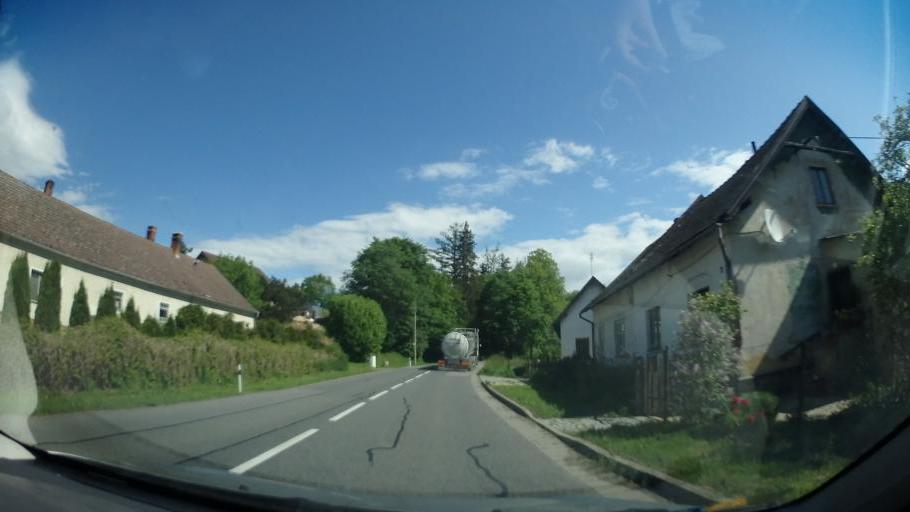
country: CZ
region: Pardubicky
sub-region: Okres Svitavy
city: Moravska Trebova
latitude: 49.7167
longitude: 16.6388
